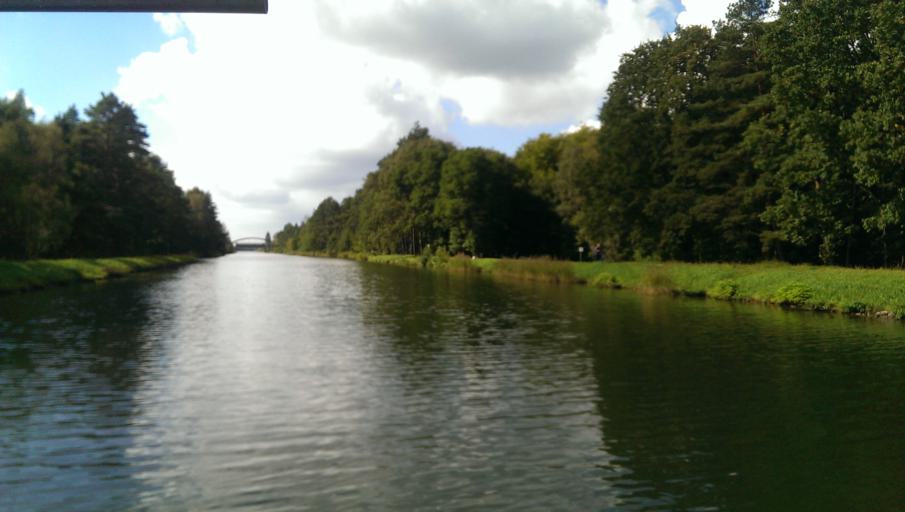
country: DE
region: Brandenburg
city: Eberswalde
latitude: 52.8590
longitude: 13.8425
